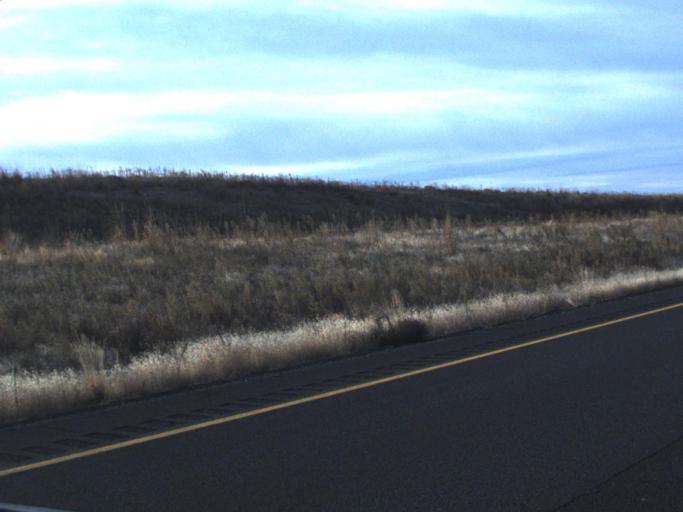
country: US
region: Washington
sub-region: Franklin County
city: Connell
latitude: 46.8566
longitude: -118.6364
